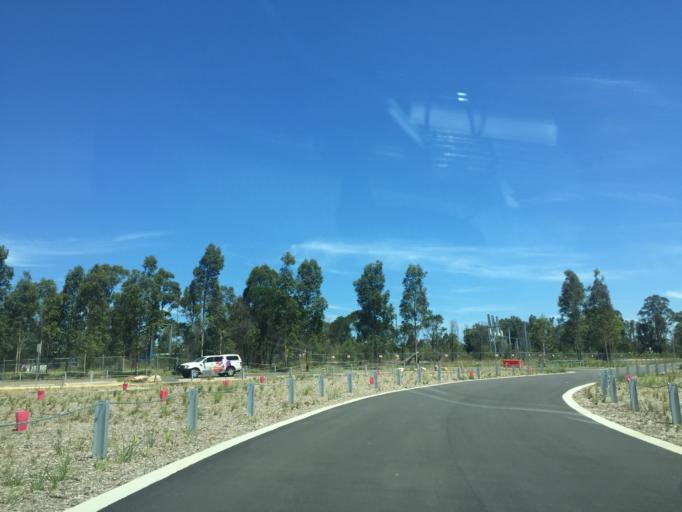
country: AU
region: New South Wales
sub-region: Blacktown
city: Doonside
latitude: -33.7856
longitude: 150.8712
